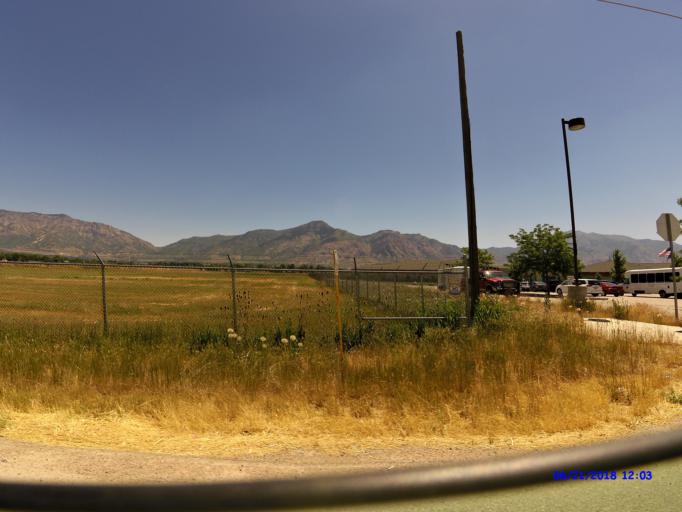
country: US
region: Utah
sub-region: Weber County
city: Harrisville
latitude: 41.2784
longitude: -112.0085
